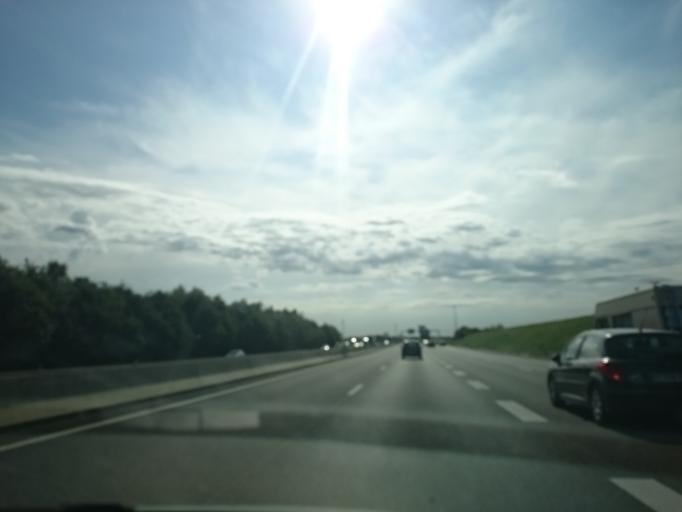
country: FR
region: Brittany
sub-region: Departement d'Ille-et-Vilaine
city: Vezin-le-Coquet
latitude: 48.1286
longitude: -1.7502
